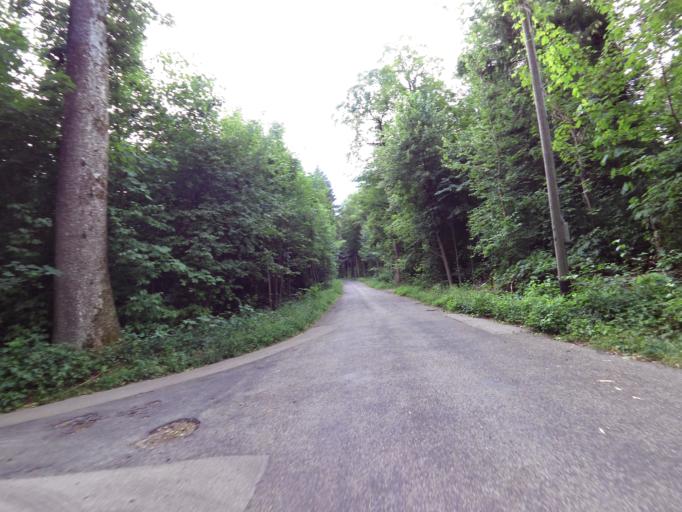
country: CH
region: Zurich
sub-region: Bezirk Zuerich
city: Zuerich (Kreis 10) / Hoengg
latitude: 47.4102
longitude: 8.4910
